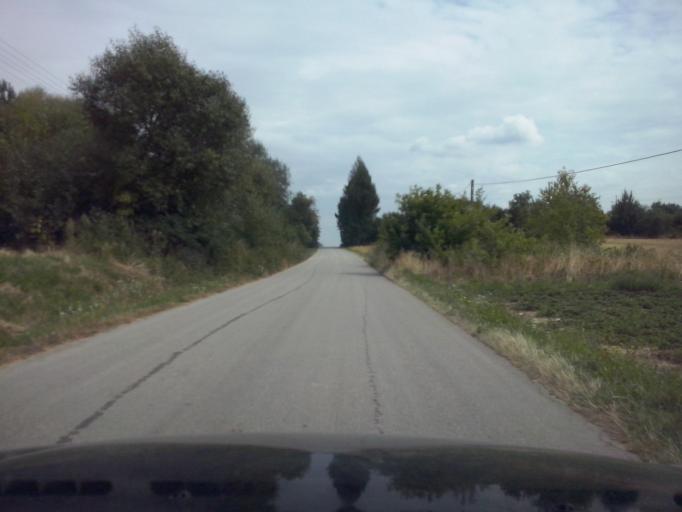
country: PL
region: Swietokrzyskie
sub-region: Powiat kielecki
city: Lagow
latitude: 50.7177
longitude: 21.1253
